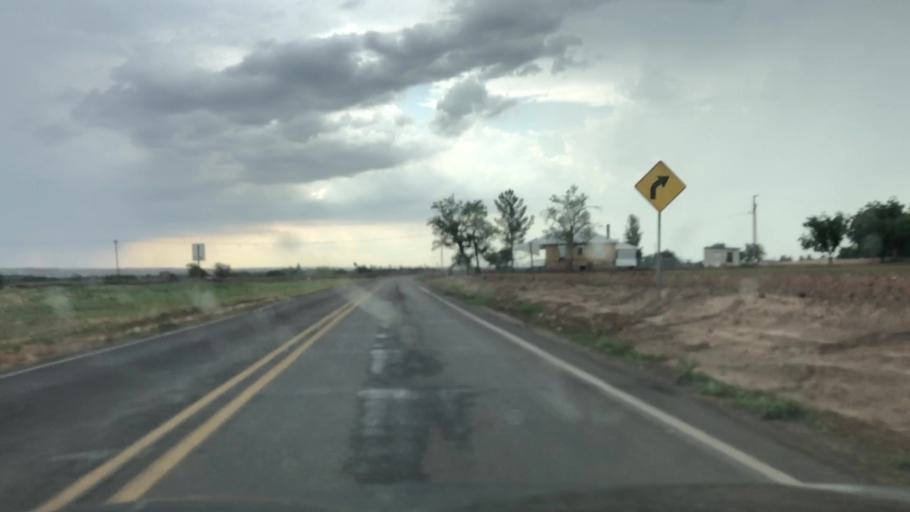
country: US
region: New Mexico
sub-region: Dona Ana County
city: Vado
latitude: 32.0697
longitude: -106.6815
